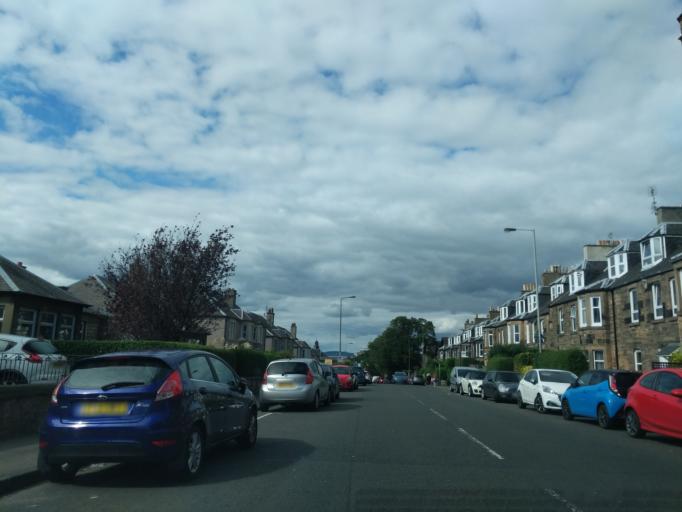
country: GB
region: Scotland
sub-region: West Lothian
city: Seafield
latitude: 55.9656
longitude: -3.1635
